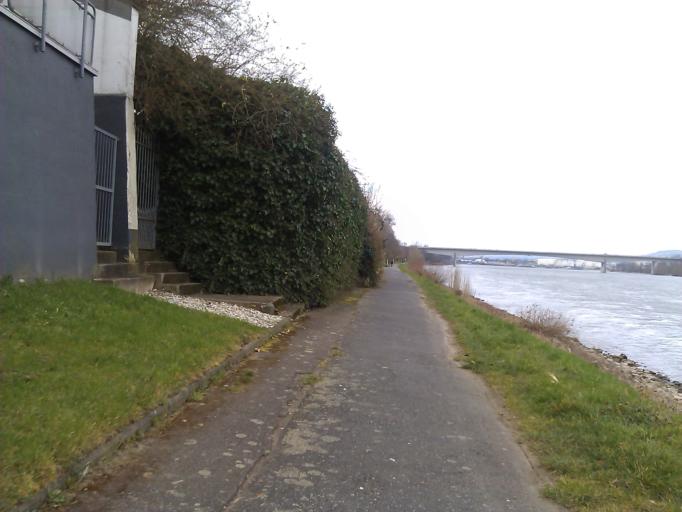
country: DE
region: Rheinland-Pfalz
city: Sankt Sebastian
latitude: 50.4015
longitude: 7.5806
